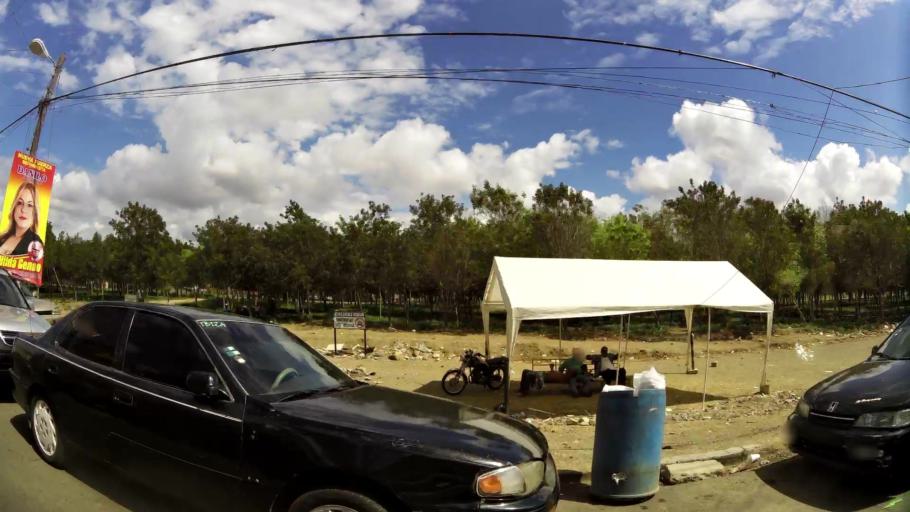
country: DO
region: Santiago
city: Santiago de los Caballeros
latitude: 19.4701
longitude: -70.7033
